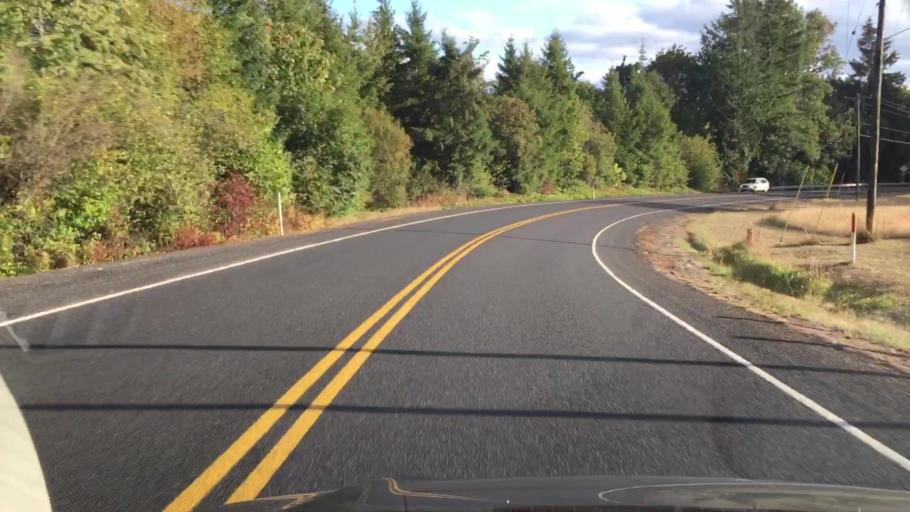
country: US
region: Washington
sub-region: Lewis County
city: Winlock
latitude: 46.4417
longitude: -122.8832
